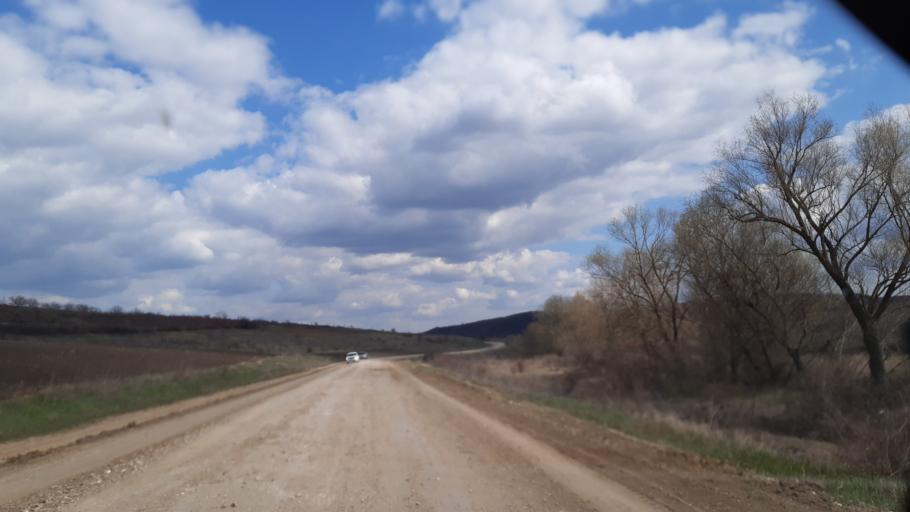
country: MD
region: Laloveni
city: Ialoveni
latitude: 46.8899
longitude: 28.7049
